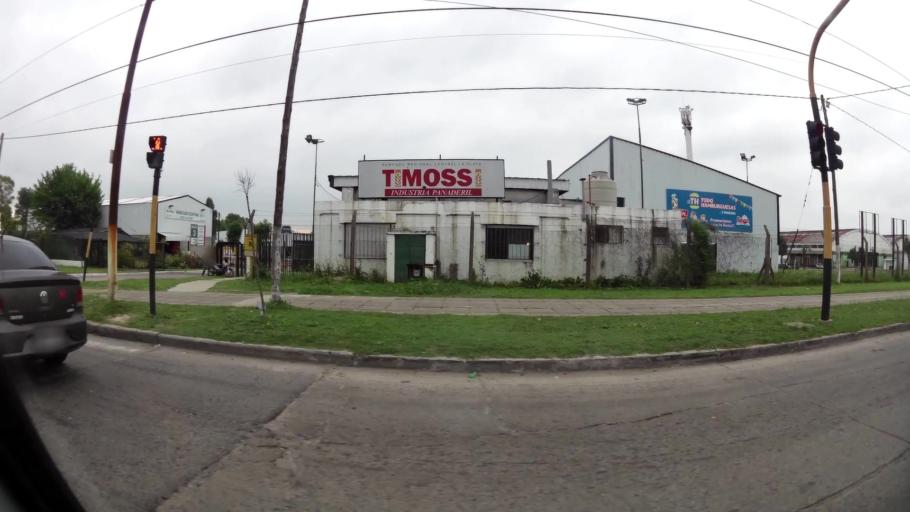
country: AR
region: Buenos Aires
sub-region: Partido de La Plata
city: La Plata
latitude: -34.8840
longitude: -57.9755
